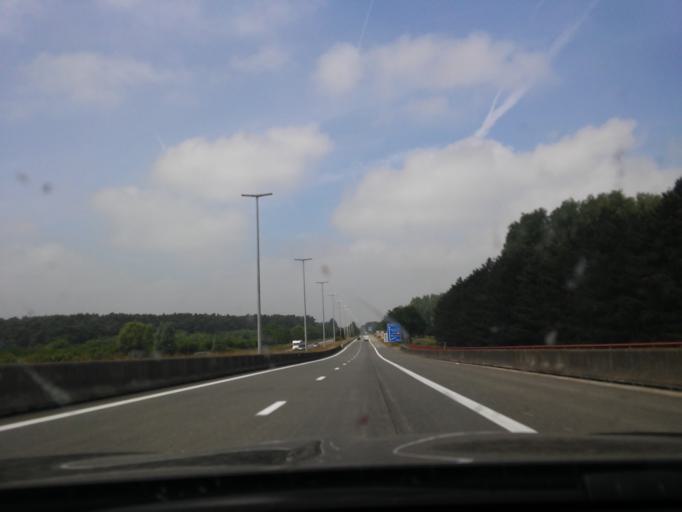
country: BE
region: Flanders
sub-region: Provincie Oost-Vlaanderen
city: Wachtebeke
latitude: 51.1883
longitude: 3.8534
